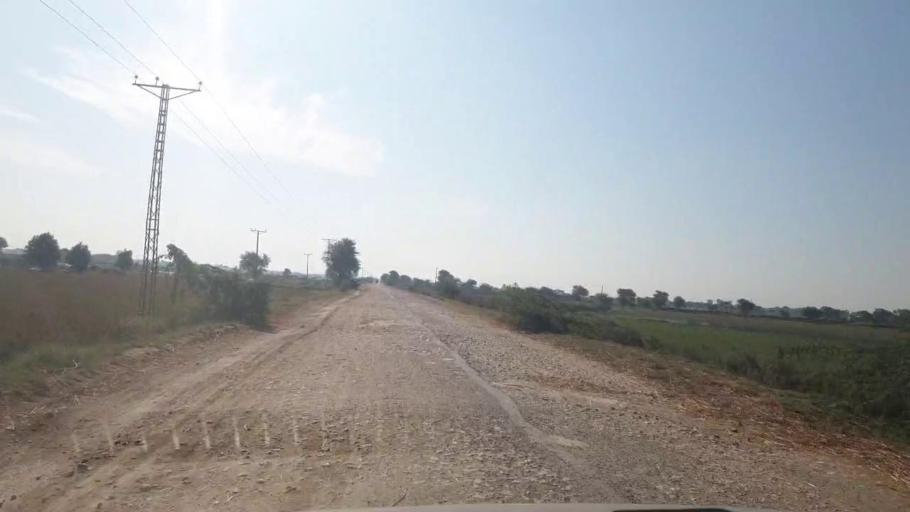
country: PK
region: Sindh
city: Talhar
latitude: 24.9123
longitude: 68.8182
